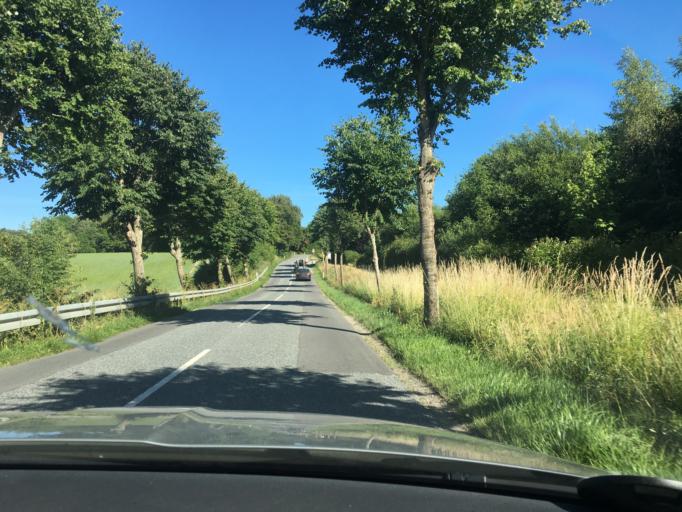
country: DK
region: Central Jutland
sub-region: Syddjurs Kommune
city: Hornslet
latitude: 56.3114
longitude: 10.3354
